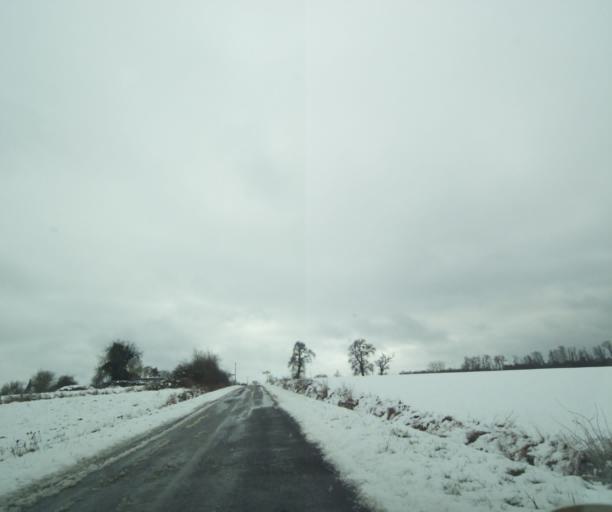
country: FR
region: Champagne-Ardenne
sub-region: Departement de la Haute-Marne
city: Montier-en-Der
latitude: 48.4154
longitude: 4.7348
